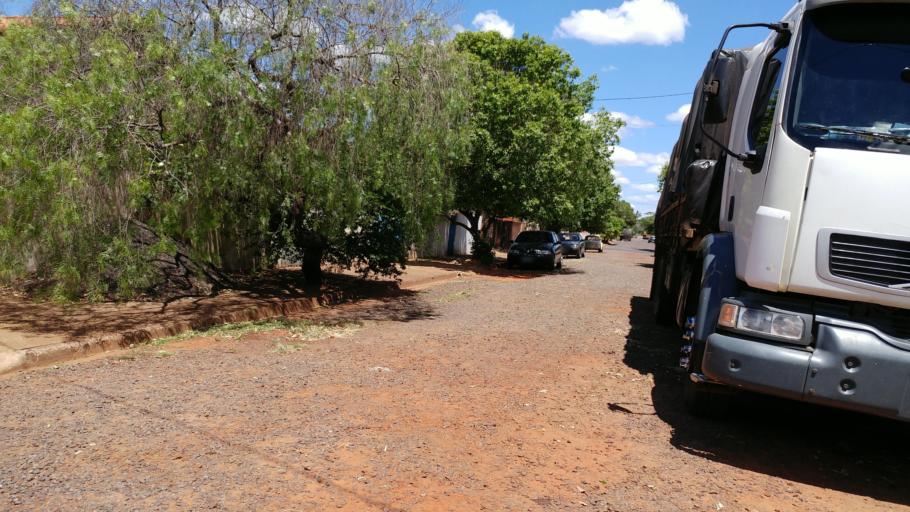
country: BR
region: Sao Paulo
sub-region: Paraguacu Paulista
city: Paraguacu Paulista
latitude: -22.4058
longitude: -50.5701
